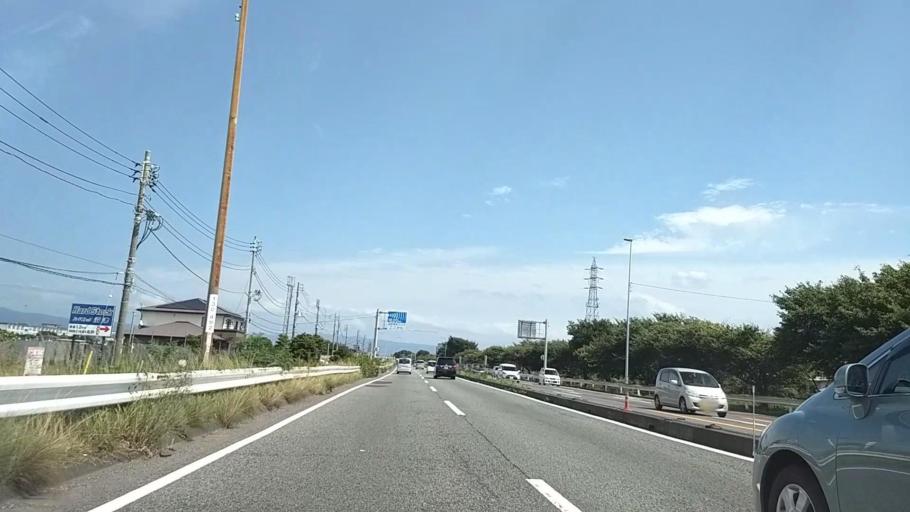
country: JP
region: Shizuoka
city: Numazu
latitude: 35.1250
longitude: 138.8102
